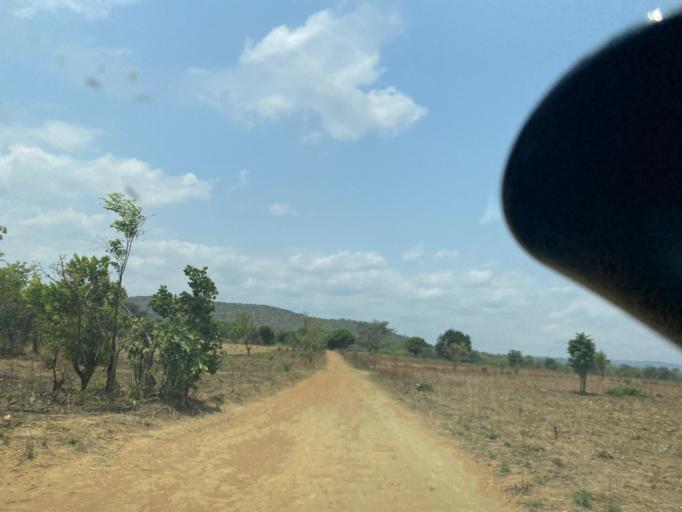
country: ZM
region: Lusaka
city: Chongwe
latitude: -15.5165
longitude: 28.8905
